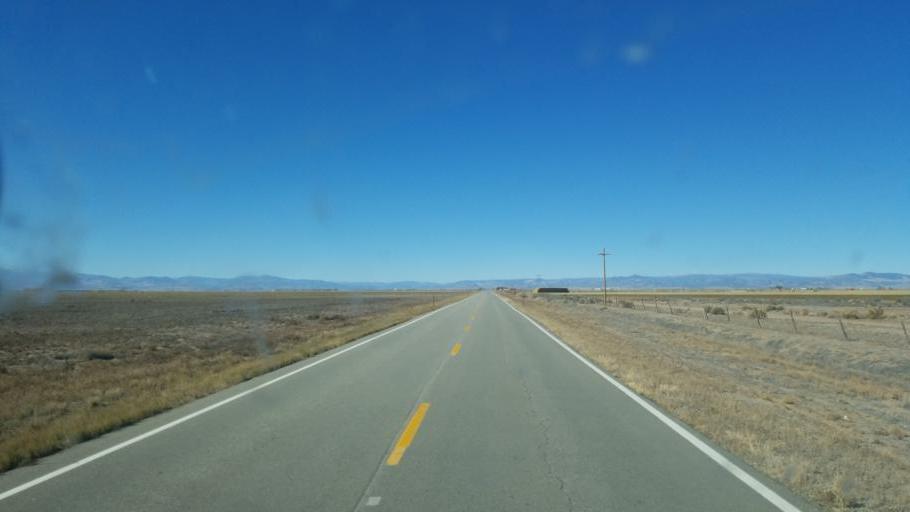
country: US
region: Colorado
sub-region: Saguache County
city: Center
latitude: 37.7489
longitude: -105.9373
